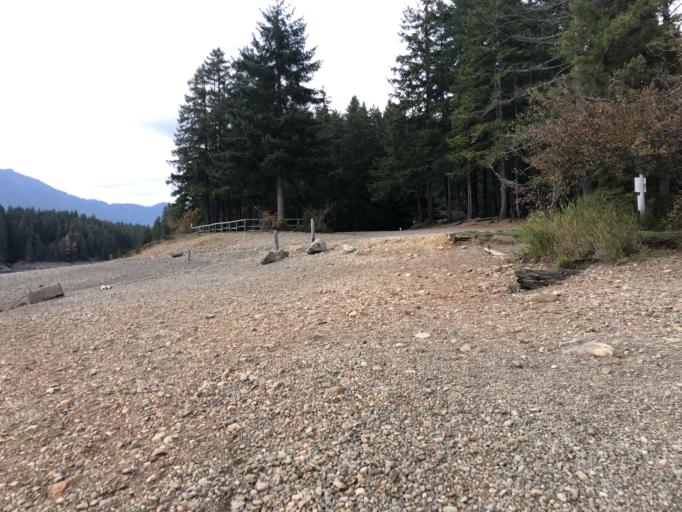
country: US
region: Washington
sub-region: Mason County
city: Shelton
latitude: 47.4644
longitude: -123.2221
